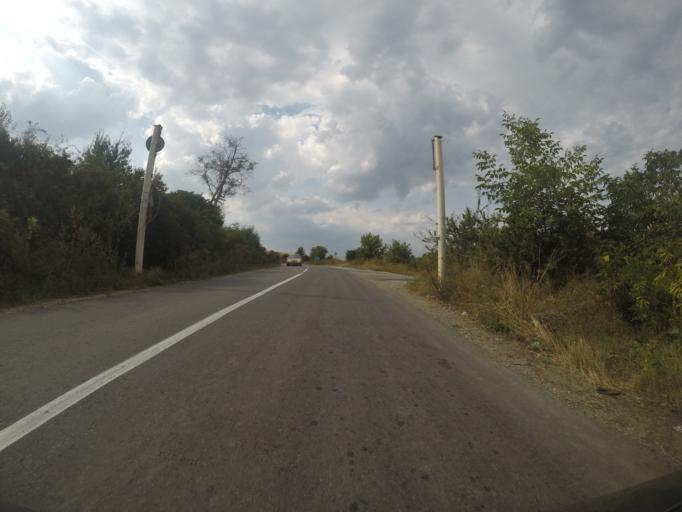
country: RO
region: Cluj
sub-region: Comuna Sandulesti
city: Copaceni
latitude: 46.5854
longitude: 23.7510
